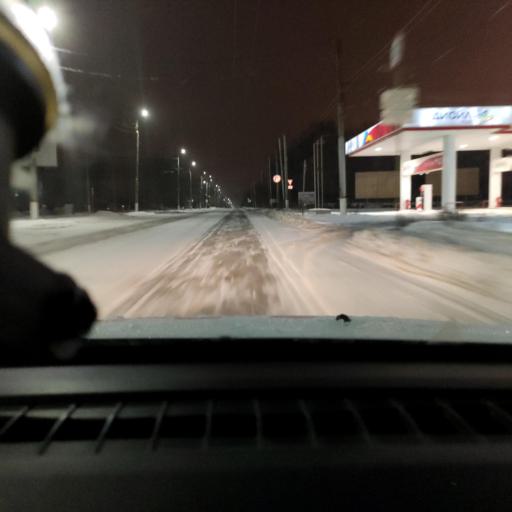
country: RU
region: Samara
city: Novokuybyshevsk
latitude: 53.0856
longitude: 49.9470
